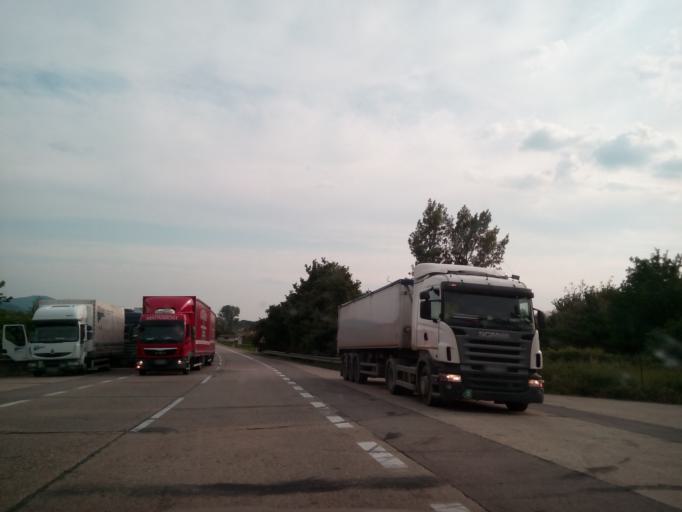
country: SK
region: Trenciansky
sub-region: Okres Trencin
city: Trencin
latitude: 48.8732
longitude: 17.9571
